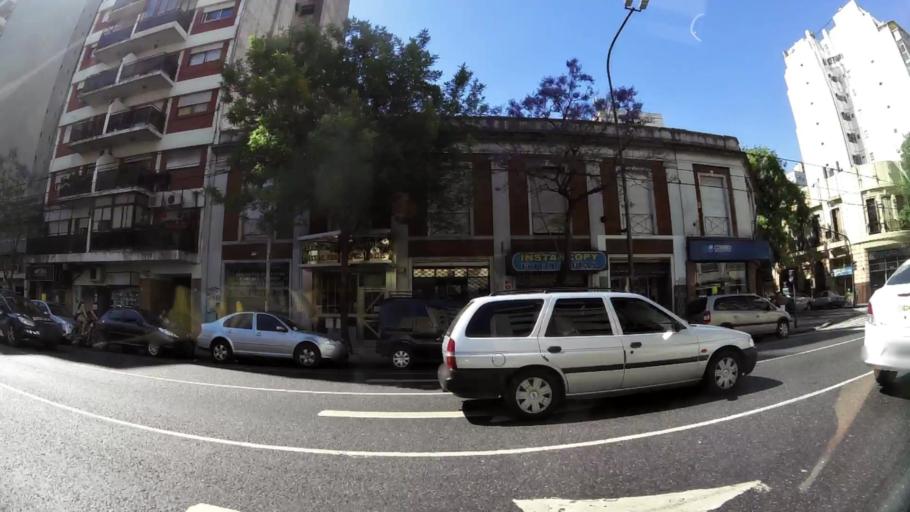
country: AR
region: Buenos Aires F.D.
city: Buenos Aires
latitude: -34.6244
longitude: -58.4074
